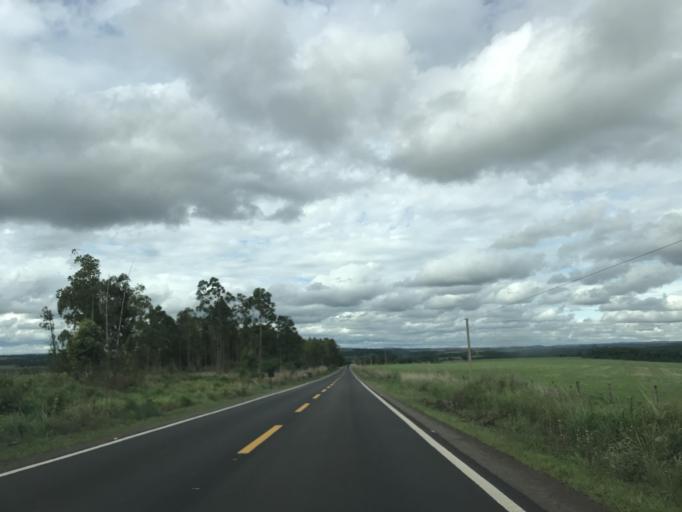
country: BR
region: Goias
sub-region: Bela Vista De Goias
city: Bela Vista de Goias
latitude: -17.1857
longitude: -48.6914
